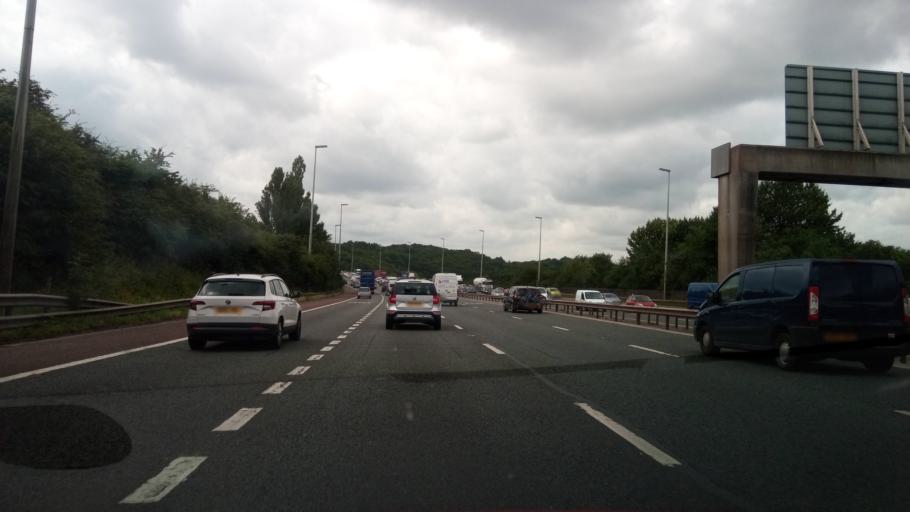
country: GB
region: England
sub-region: Lancashire
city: Clayton-le-Woods
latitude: 53.7470
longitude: -2.6477
